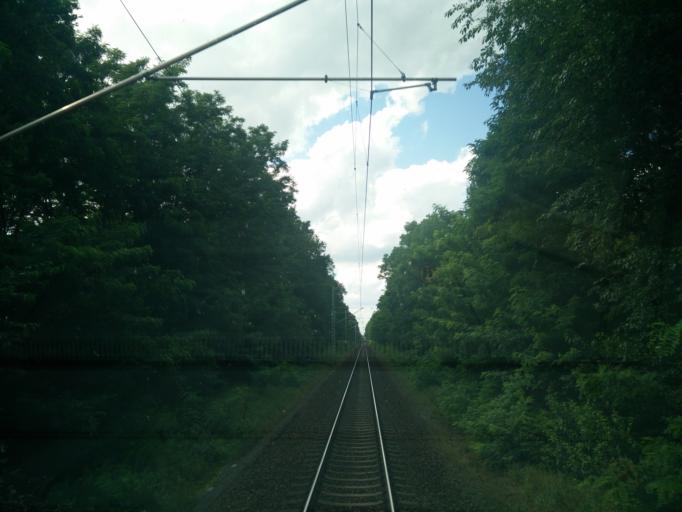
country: DE
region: Brandenburg
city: Vetschau
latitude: 51.7935
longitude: 14.0694
